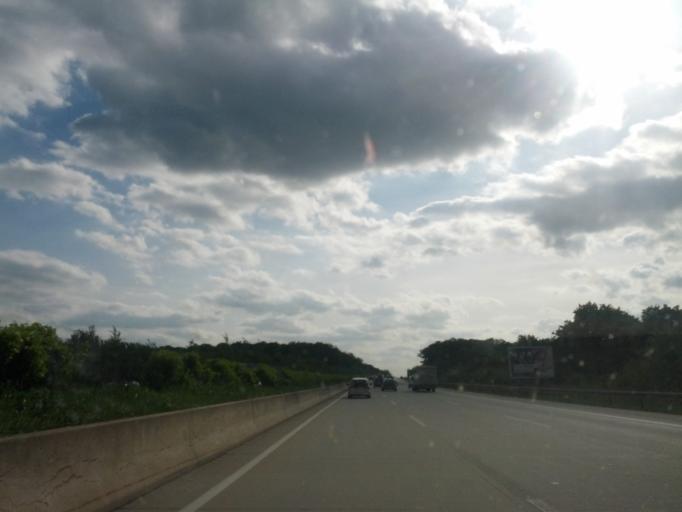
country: DE
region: Thuringia
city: Klettbach
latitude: 50.9209
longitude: 11.1149
